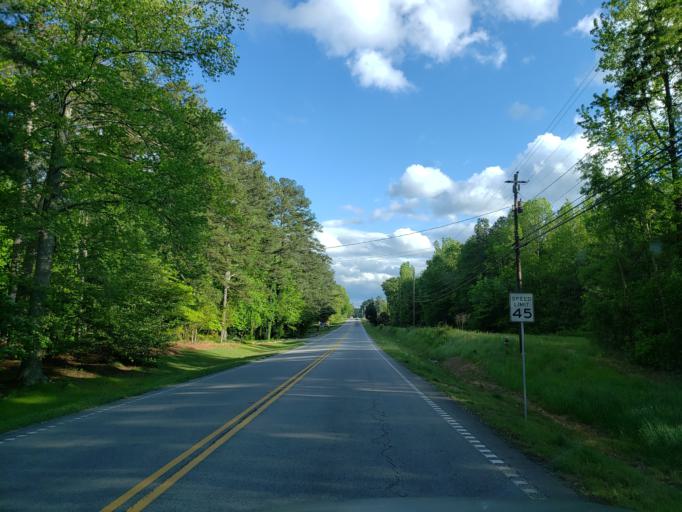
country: US
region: Georgia
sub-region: Haralson County
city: Tallapoosa
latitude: 33.7653
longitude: -85.2950
